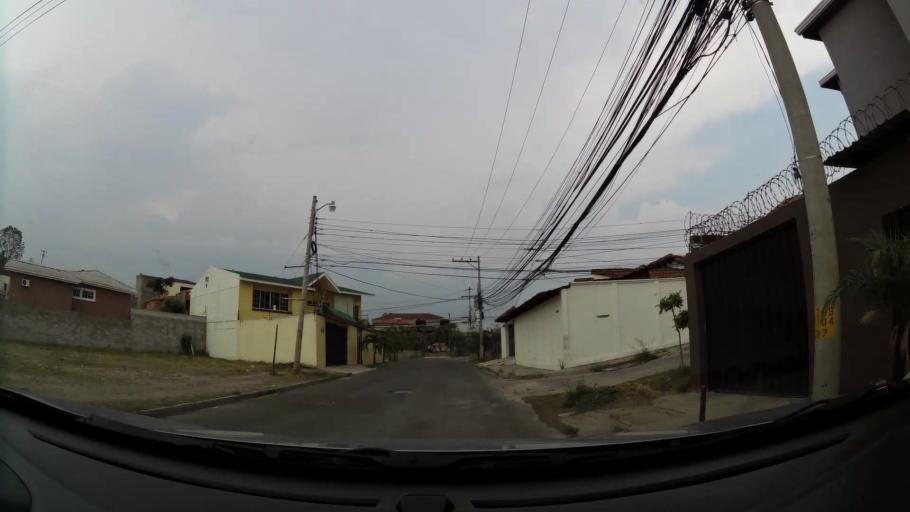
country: HN
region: Francisco Morazan
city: Tegucigalpa
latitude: 14.0535
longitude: -87.2325
